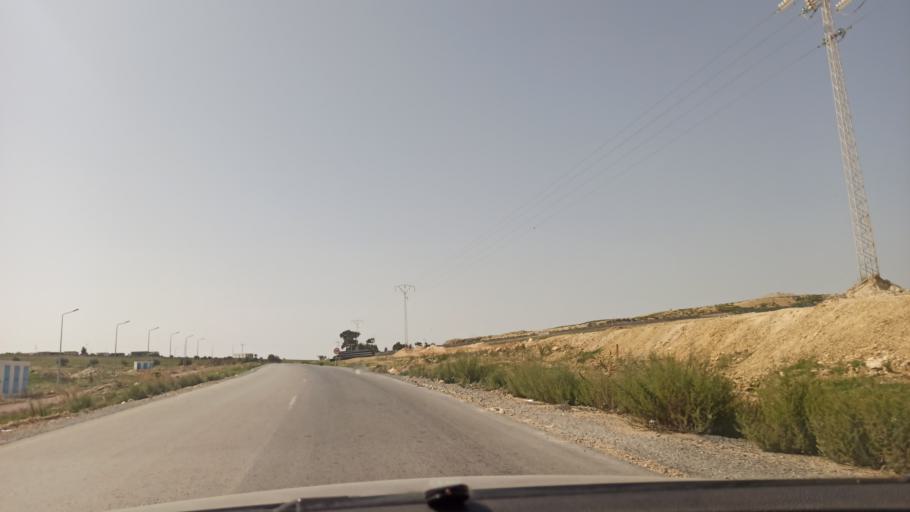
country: TN
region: Manouba
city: Manouba
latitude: 36.7394
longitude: 10.0857
